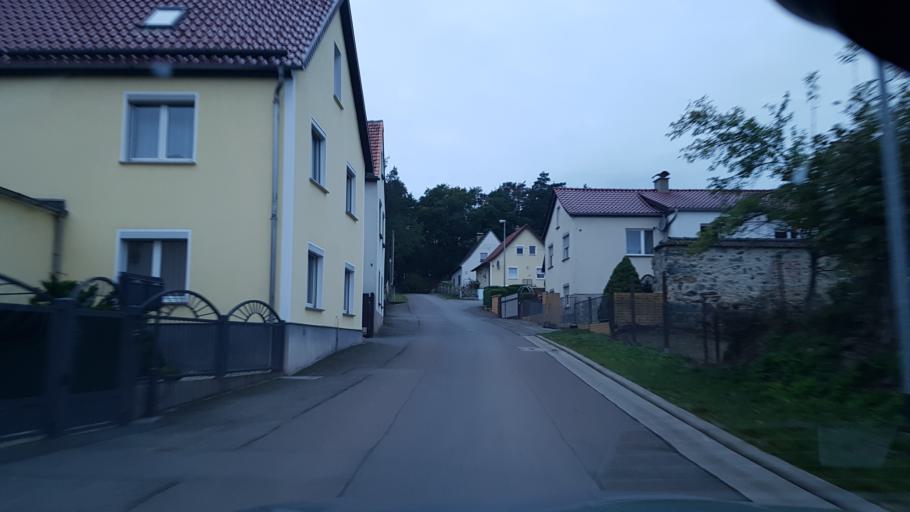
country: DE
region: Brandenburg
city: Hirschfeld
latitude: 51.3836
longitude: 13.6136
